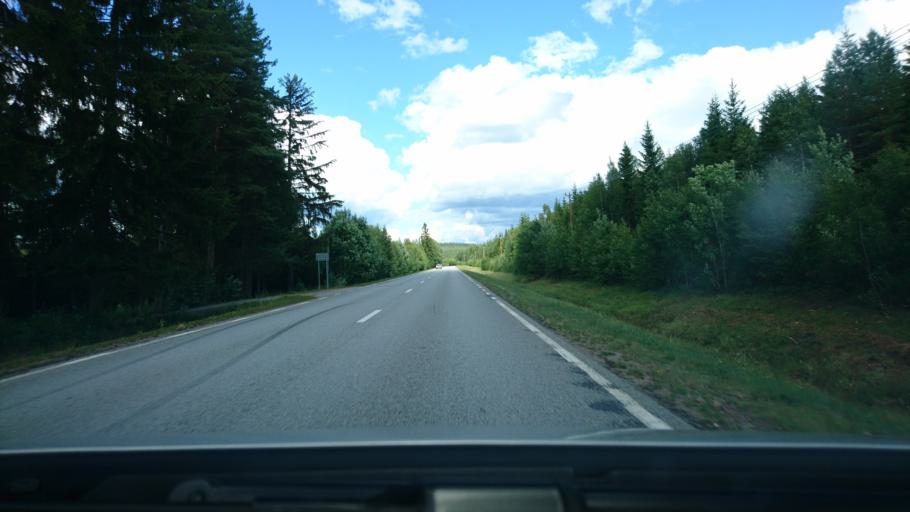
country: SE
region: Vaesternorrland
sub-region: Solleftea Kommun
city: As
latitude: 63.7068
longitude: 16.9337
